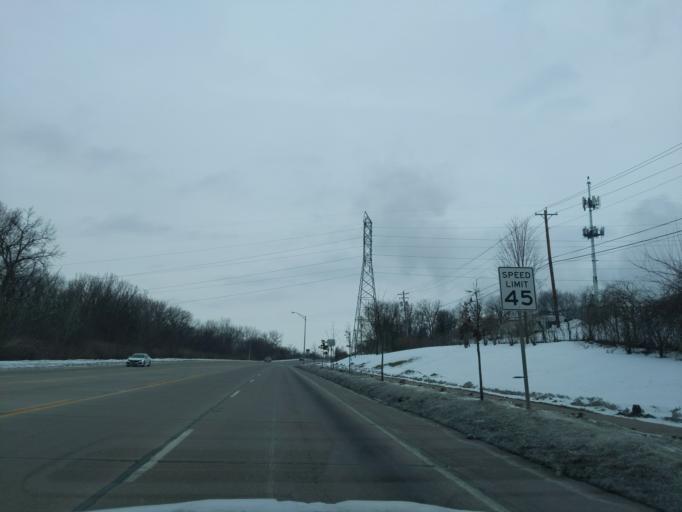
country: US
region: Indiana
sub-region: Tippecanoe County
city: West Lafayette
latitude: 40.4158
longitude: -86.9088
